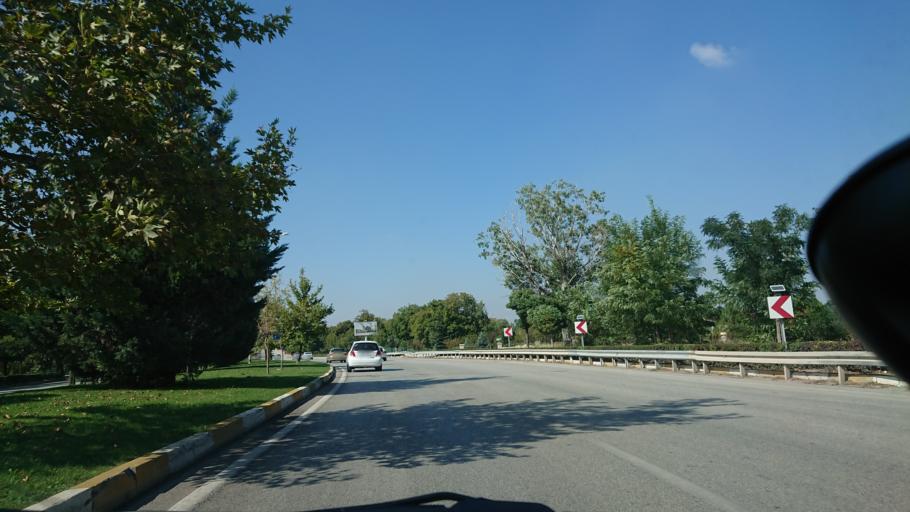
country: TR
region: Eskisehir
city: Eskisehir
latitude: 39.7575
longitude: 30.4815
